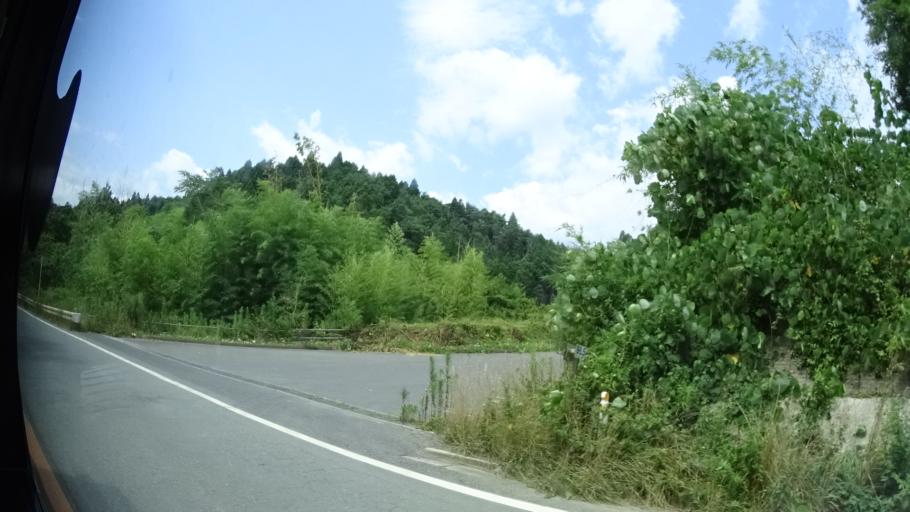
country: JP
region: Miyagi
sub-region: Oshika Gun
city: Onagawa Cho
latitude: 38.6961
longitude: 141.4919
